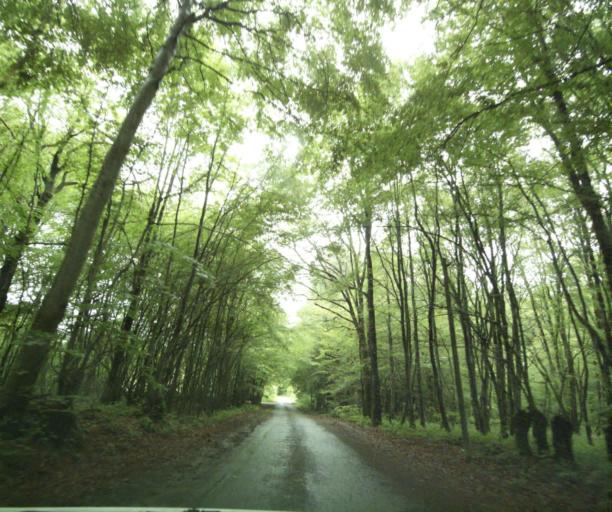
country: FR
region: Bourgogne
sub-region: Departement de Saone-et-Loire
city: Ciry-le-Noble
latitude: 46.5218
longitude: 4.3025
